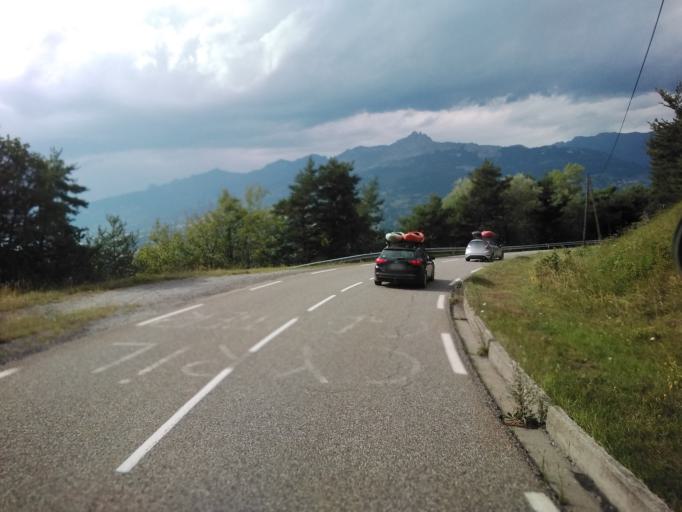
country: FR
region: Provence-Alpes-Cote d'Azur
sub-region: Departement des Hautes-Alpes
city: Chorges
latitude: 44.5047
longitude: 6.3491
